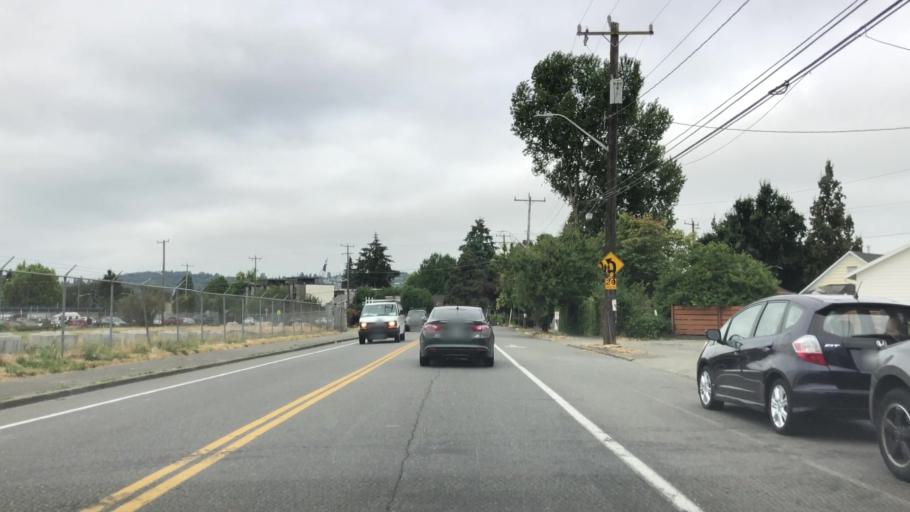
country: US
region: Washington
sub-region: King County
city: White Center
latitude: 47.5461
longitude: -122.3171
